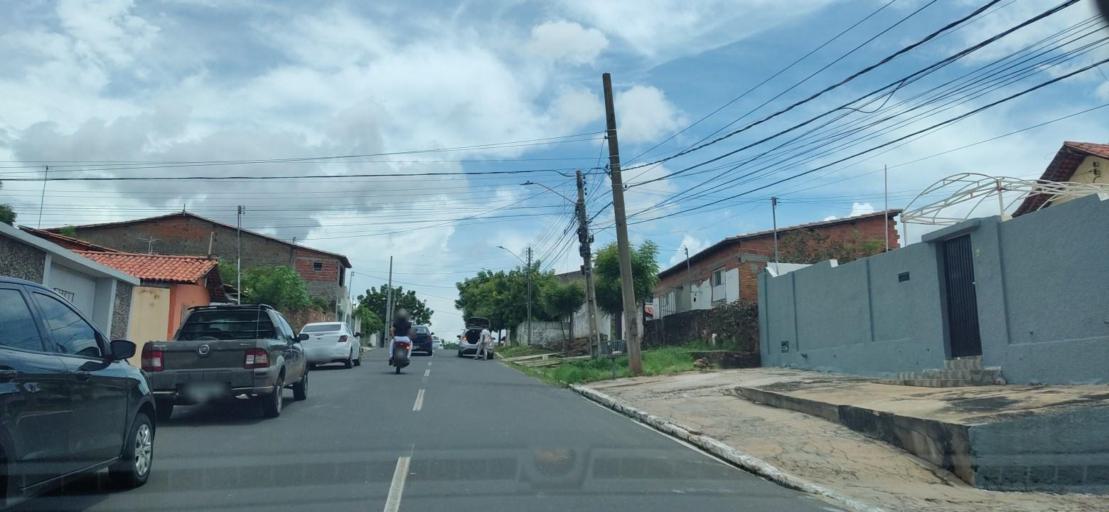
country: BR
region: Piaui
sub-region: Teresina
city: Teresina
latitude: -5.0729
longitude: -42.8042
